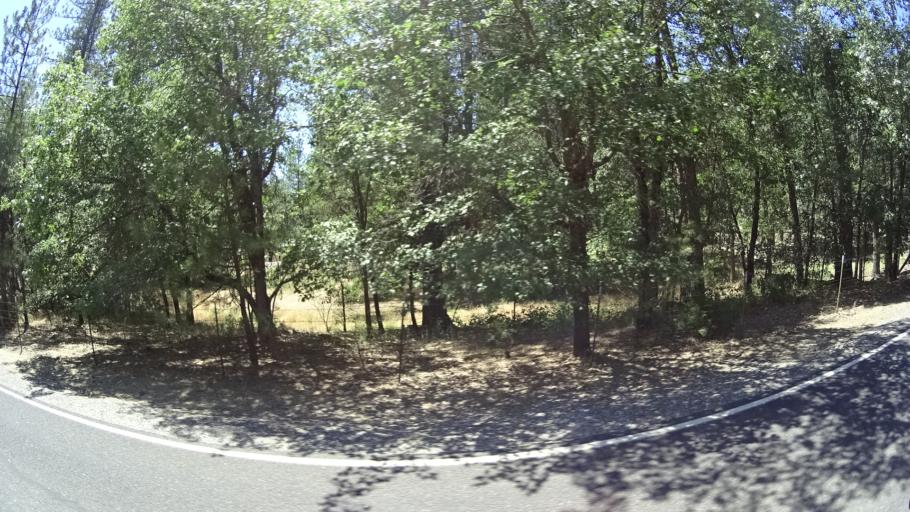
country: US
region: California
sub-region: Calaveras County
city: Mountain Ranch
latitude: 38.3179
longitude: -120.5207
